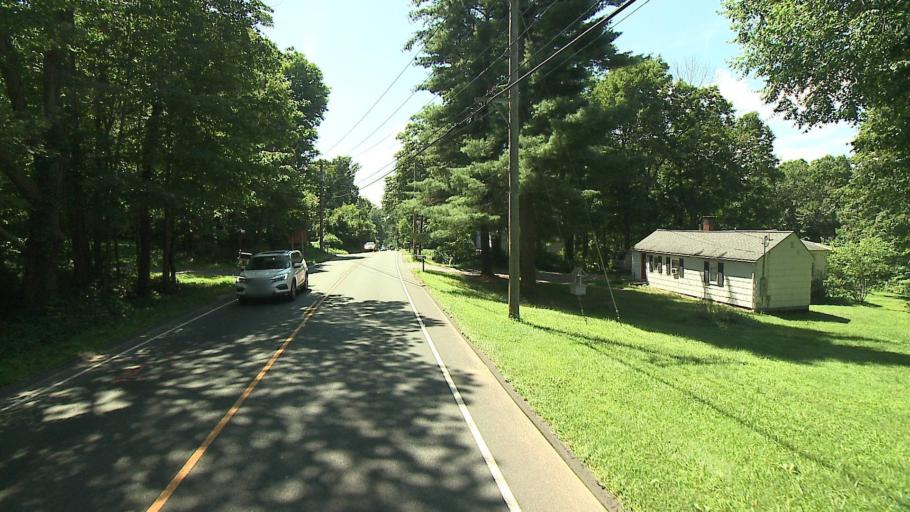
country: US
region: Connecticut
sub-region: Fairfield County
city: Trumbull
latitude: 41.3267
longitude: -73.2093
